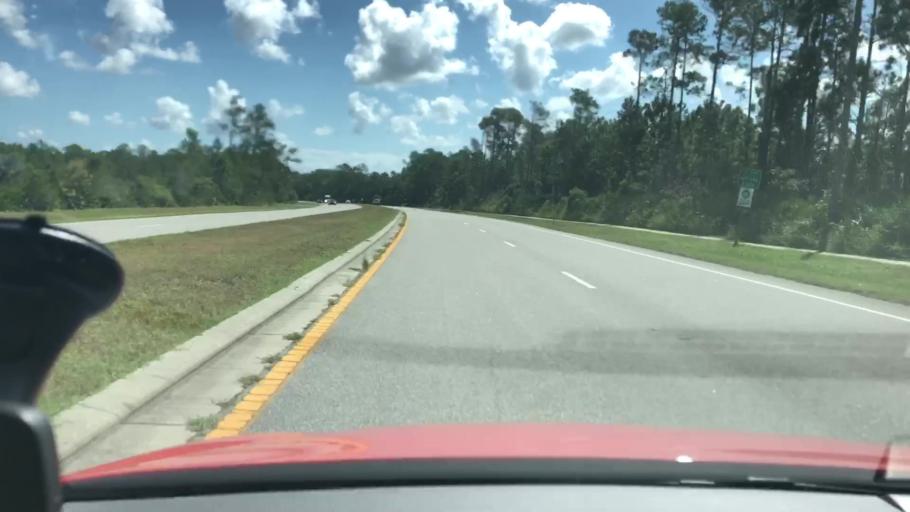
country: US
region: Florida
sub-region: Volusia County
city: Ormond Beach
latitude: 29.2464
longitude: -81.0938
